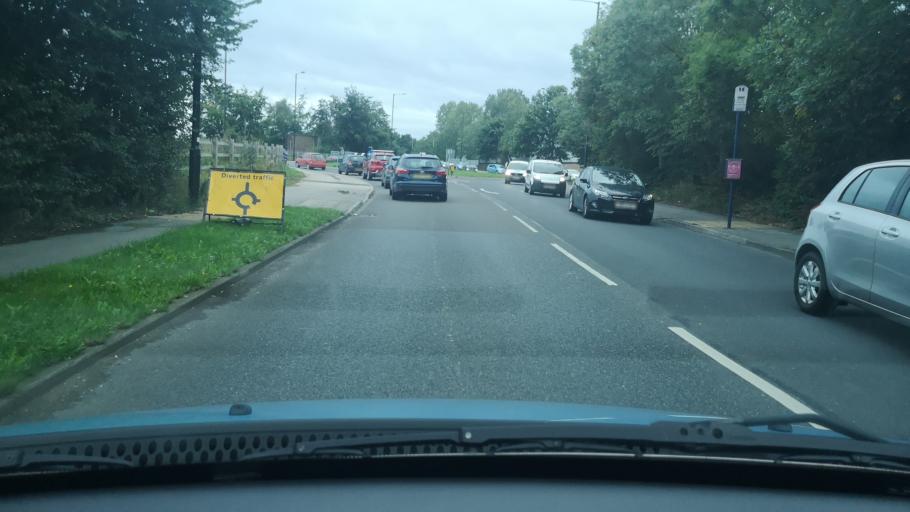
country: GB
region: England
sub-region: Doncaster
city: Kirk Sandall
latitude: 53.5547
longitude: -1.0810
